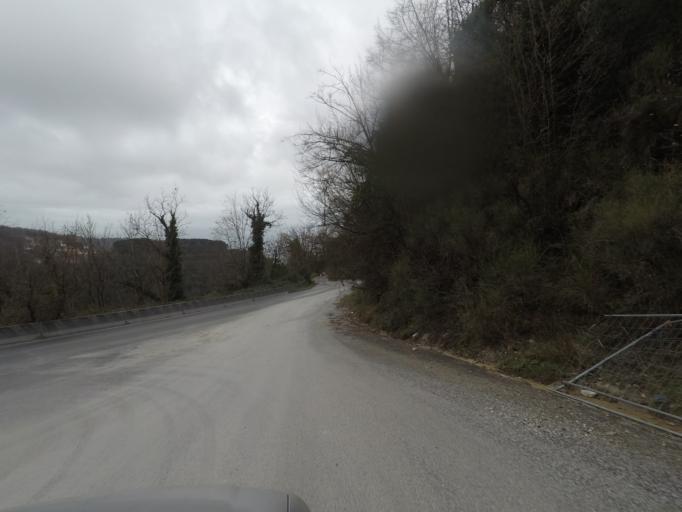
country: IT
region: Tuscany
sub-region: Provincia di Massa-Carrara
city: Carrara
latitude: 44.0850
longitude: 10.1139
